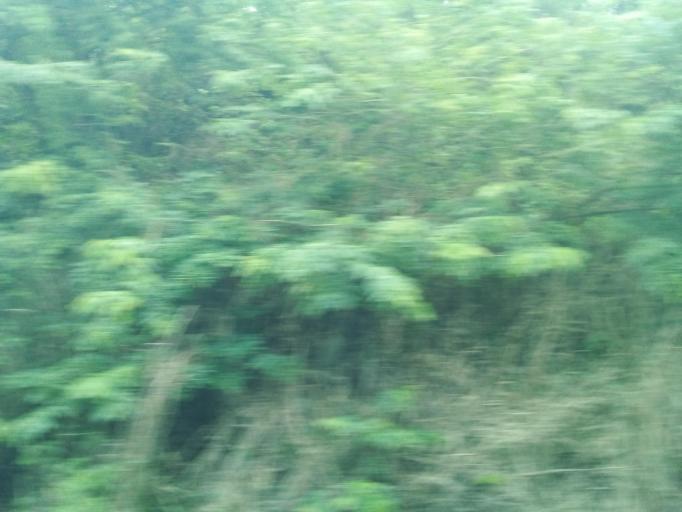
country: BR
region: Minas Gerais
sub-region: Ipaba
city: Ipaba
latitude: -19.4617
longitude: -42.4664
